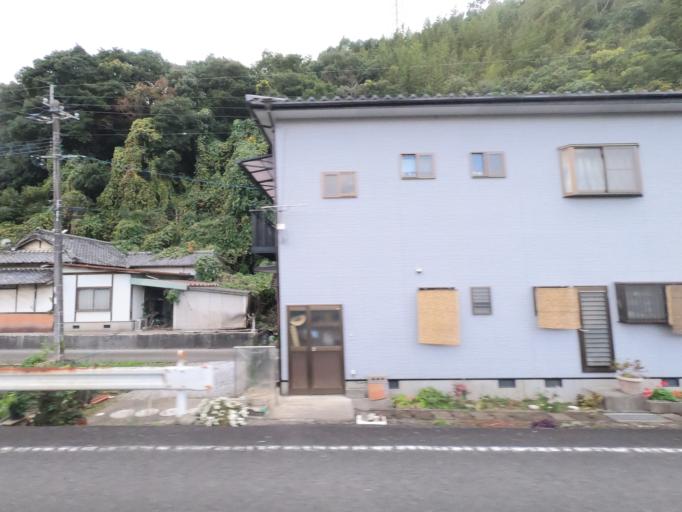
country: JP
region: Kumamoto
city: Minamata
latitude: 32.2648
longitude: 130.5069
